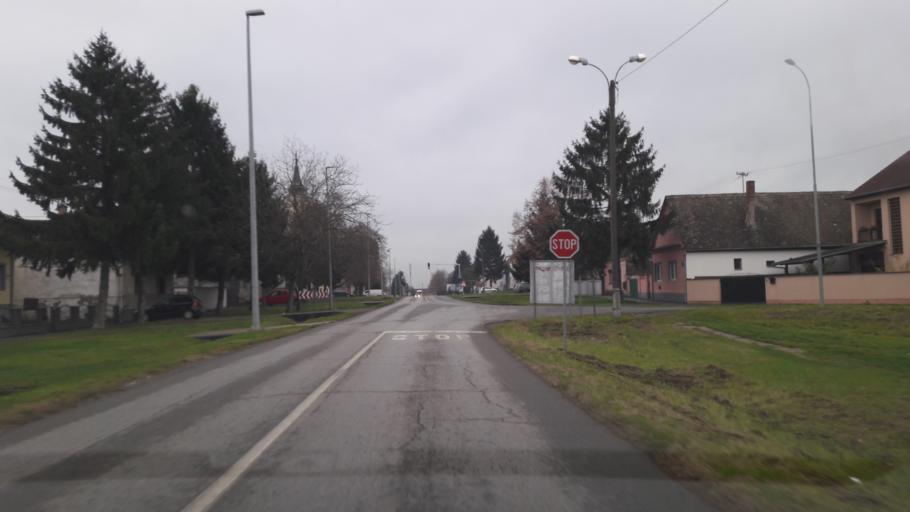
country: HR
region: Osjecko-Baranjska
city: Josipovac
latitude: 45.5829
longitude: 18.5819
